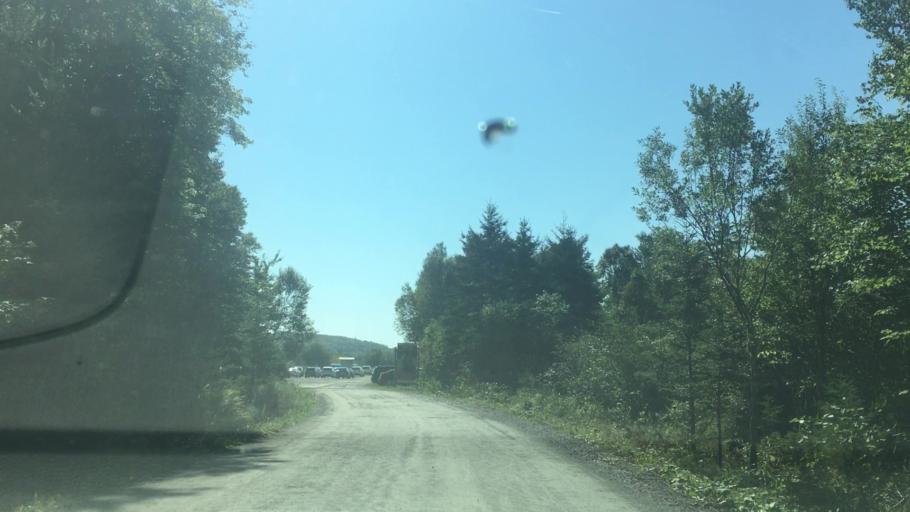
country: CA
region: Nova Scotia
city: Antigonish
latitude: 45.1394
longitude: -61.9830
